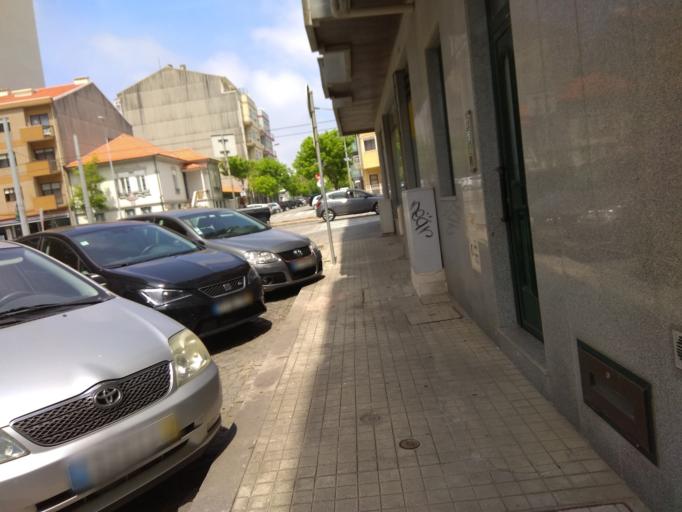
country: PT
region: Porto
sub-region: Matosinhos
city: Matosinhos
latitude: 41.1801
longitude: -8.6847
